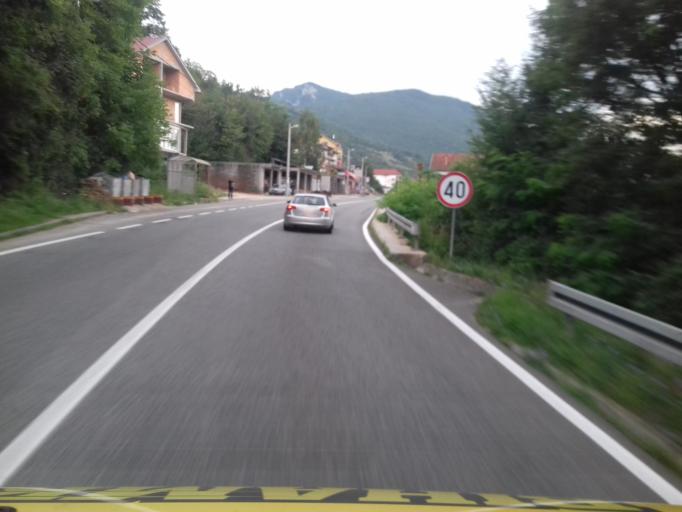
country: BA
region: Federation of Bosnia and Herzegovina
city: Jablanica
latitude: 43.6829
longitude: 17.8292
